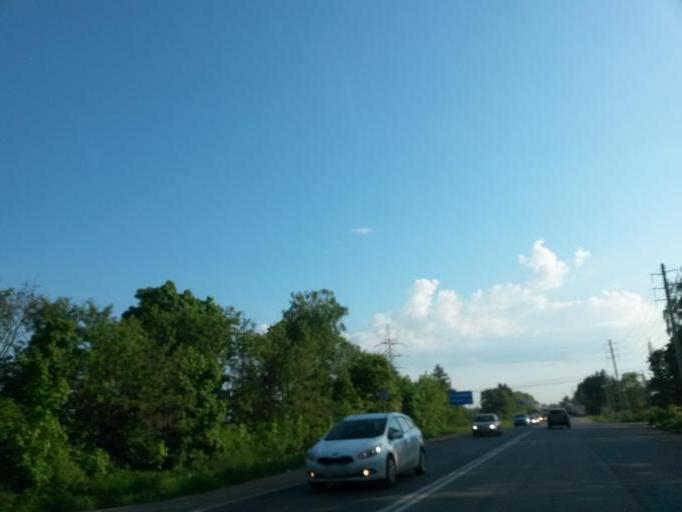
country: RU
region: Moskovskaya
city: Yam
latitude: 55.4725
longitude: 37.7116
